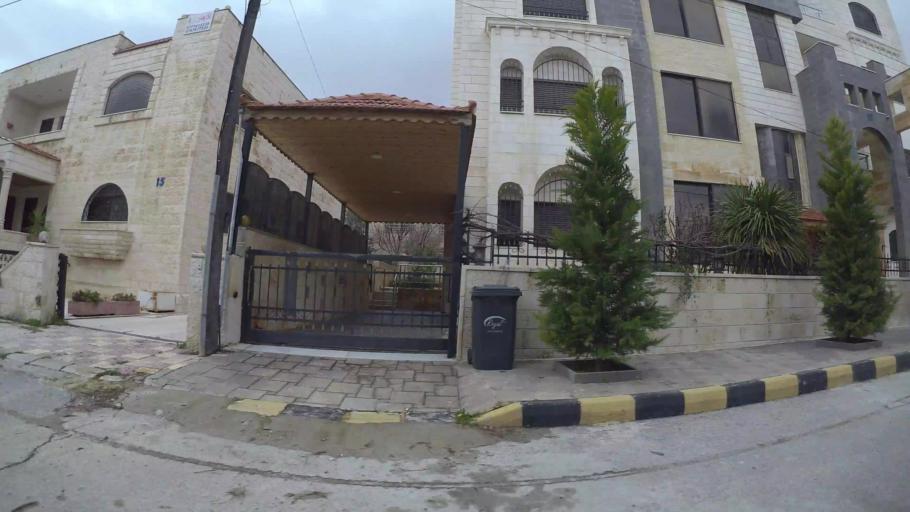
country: JO
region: Amman
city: Wadi as Sir
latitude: 31.9661
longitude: 35.8299
